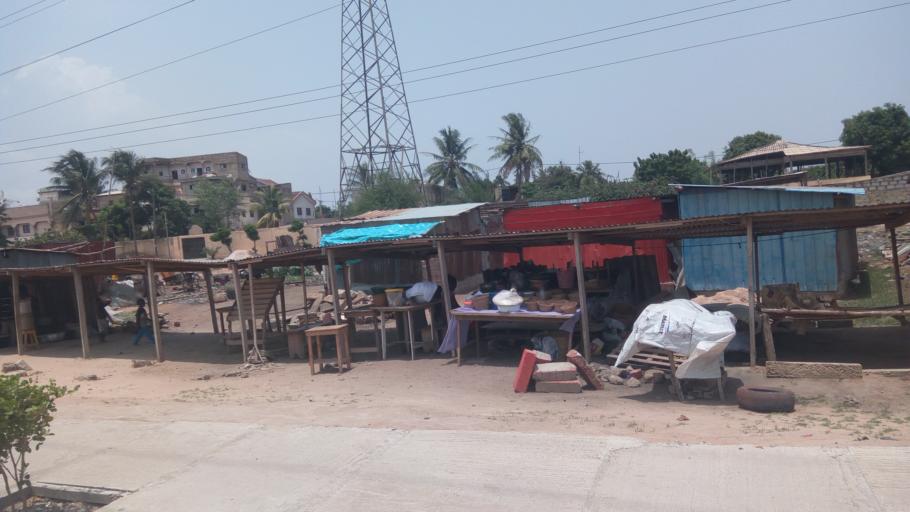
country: TG
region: Maritime
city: Lome
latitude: 6.1834
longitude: 1.2032
